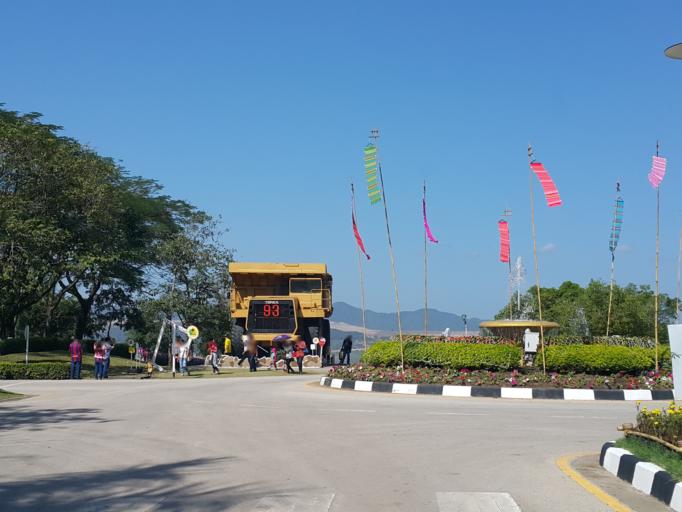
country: TH
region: Lampang
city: Mae Mo
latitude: 18.3186
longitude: 99.7438
